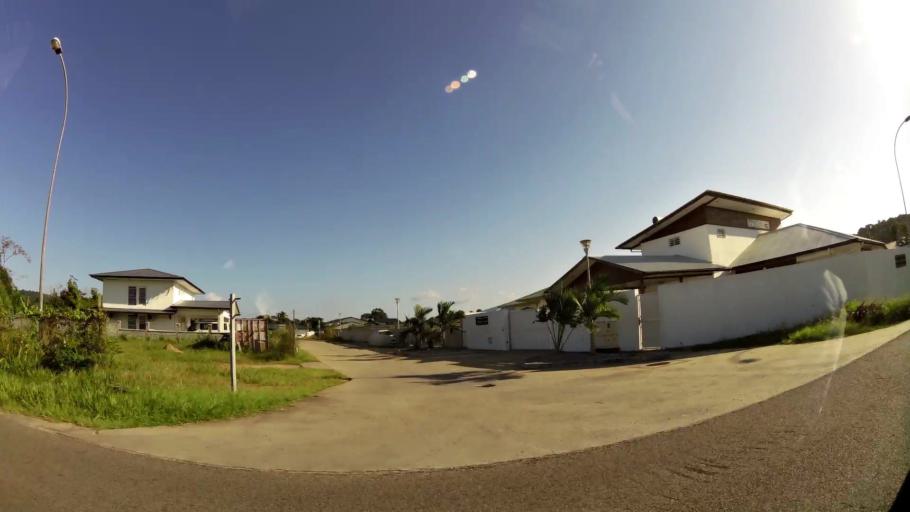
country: GF
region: Guyane
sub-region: Guyane
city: Remire-Montjoly
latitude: 4.9022
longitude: -52.2805
